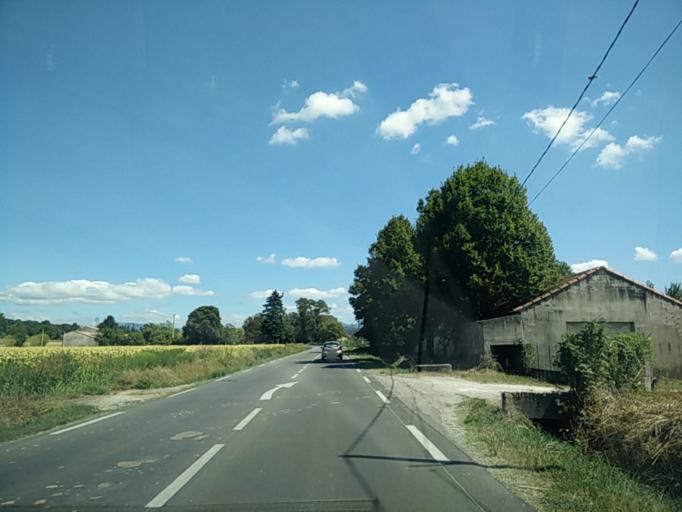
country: FR
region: Rhone-Alpes
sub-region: Departement de la Drome
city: Montboucher-sur-Jabron
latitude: 44.5496
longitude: 4.7826
